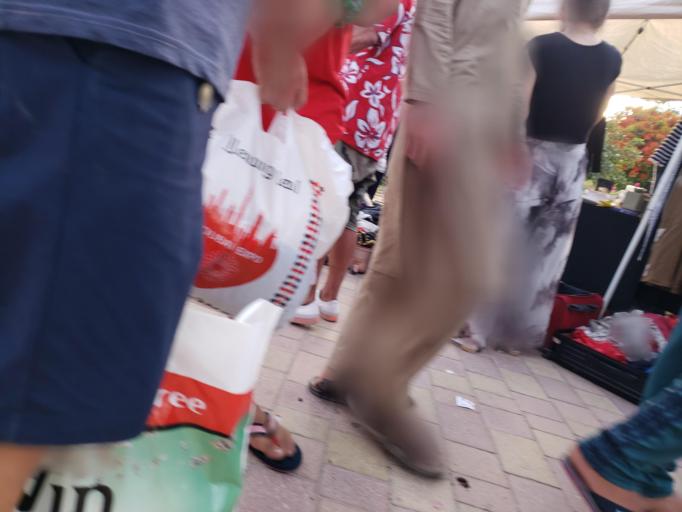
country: AE
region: Dubai
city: Dubai
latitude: 25.1030
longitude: 55.2022
